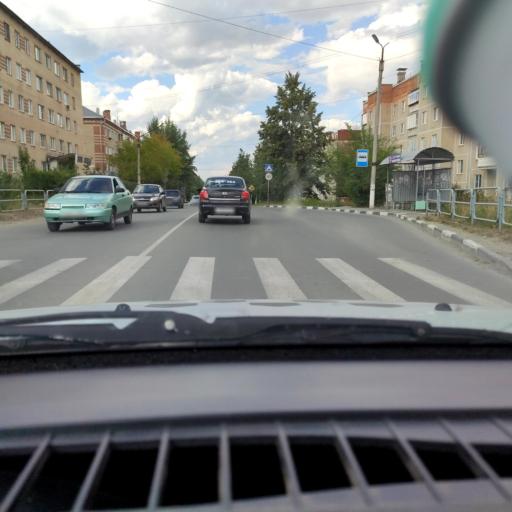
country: RU
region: Chelyabinsk
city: Miass
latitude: 55.0789
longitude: 60.0937
